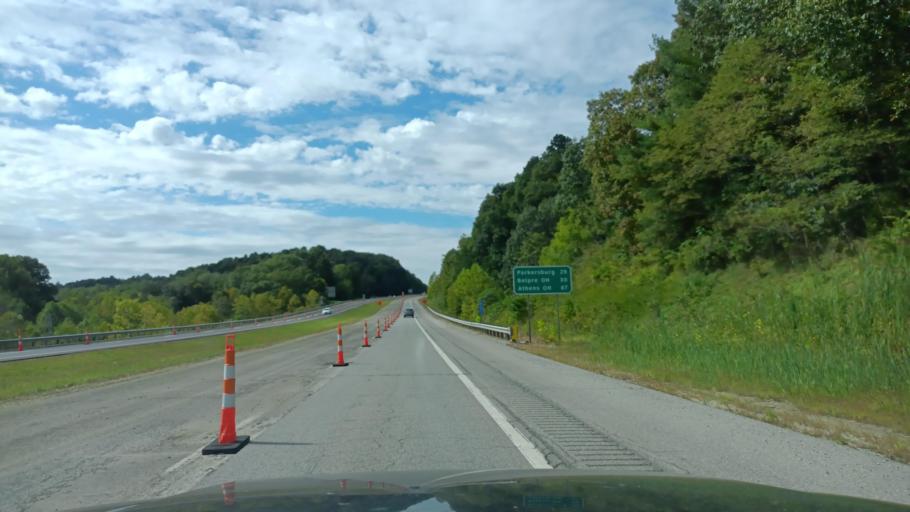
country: US
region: West Virginia
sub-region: Ritchie County
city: Harrisville
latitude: 39.2601
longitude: -81.0775
